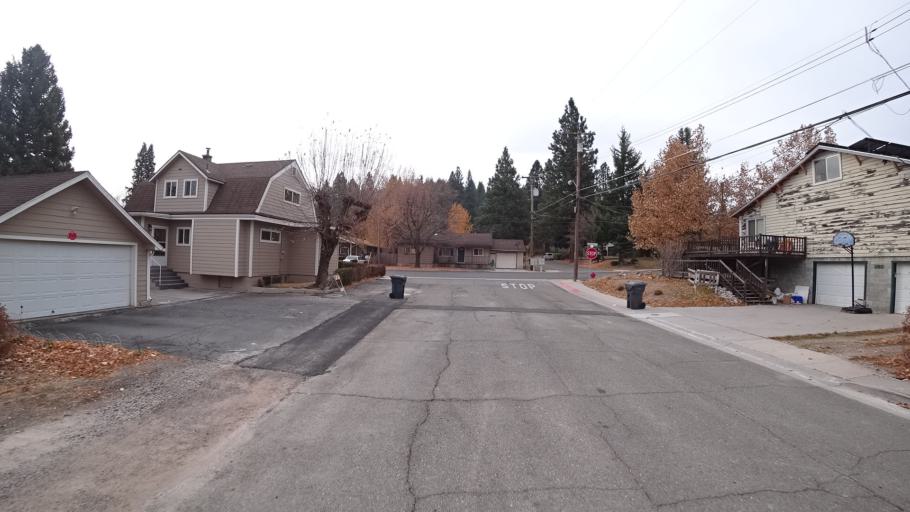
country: US
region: California
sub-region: Siskiyou County
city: Weed
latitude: 41.4145
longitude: -122.3857
